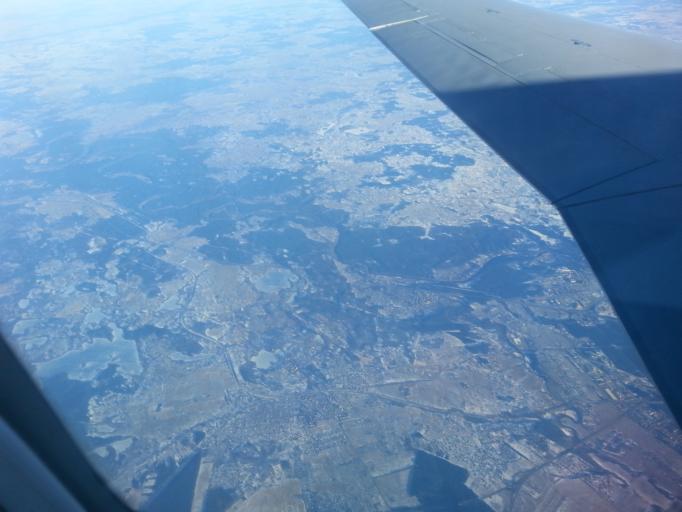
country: LT
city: Lentvaris
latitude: 54.5705
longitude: 25.0469
